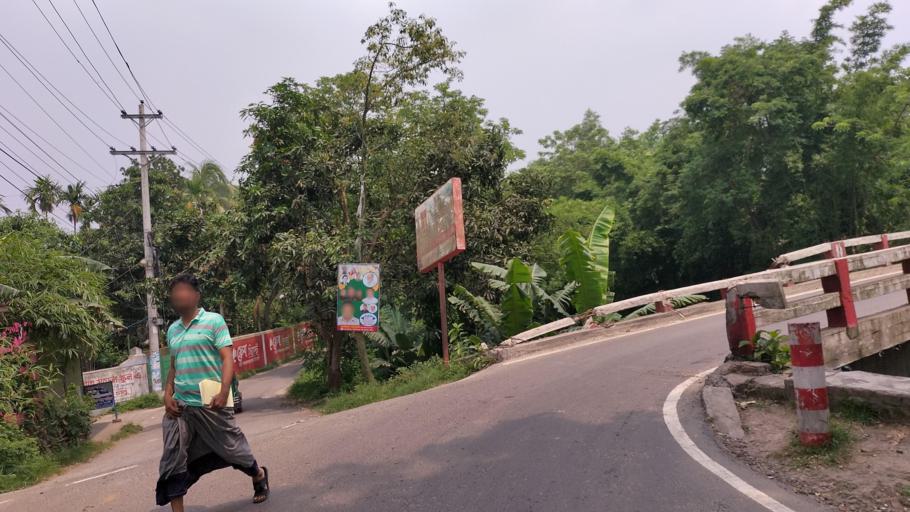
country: BD
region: Dhaka
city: Azimpur
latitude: 23.7204
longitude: 90.2759
